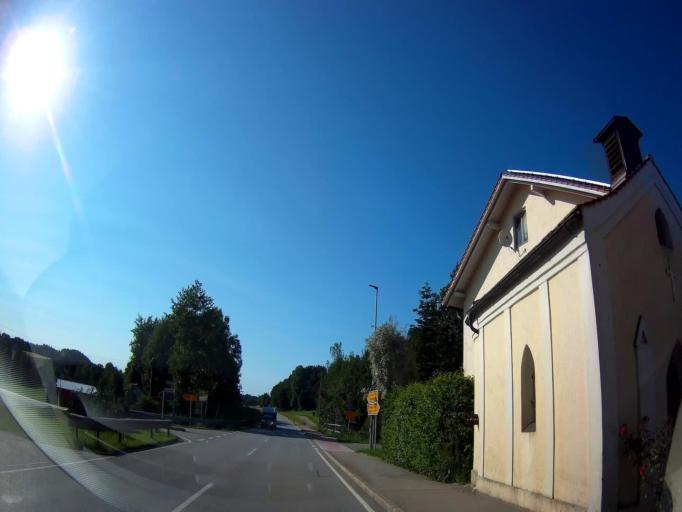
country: DE
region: Bavaria
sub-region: Lower Bavaria
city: Zeilarn
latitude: 48.2842
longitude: 12.8645
